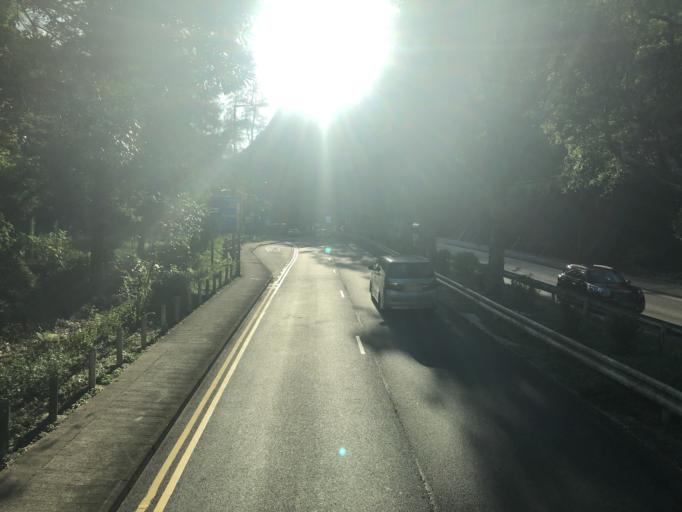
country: HK
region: Wong Tai Sin
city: Wong Tai Sin
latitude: 22.3343
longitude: 114.2313
